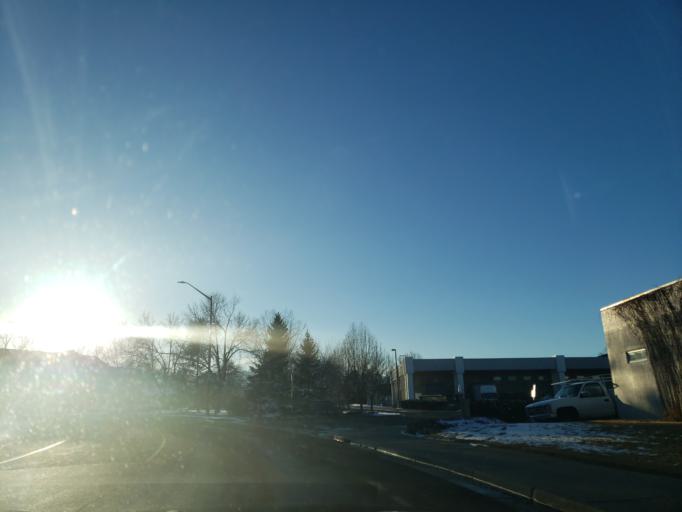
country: US
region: Colorado
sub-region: Larimer County
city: Fort Collins
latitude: 40.5767
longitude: -105.1052
